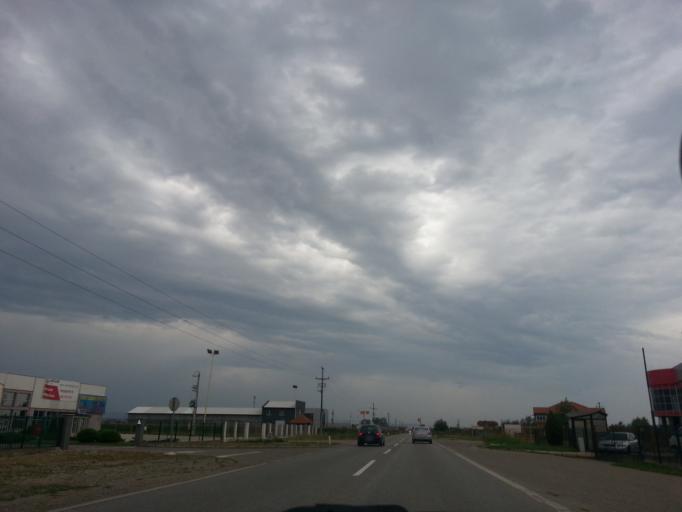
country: BA
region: Republika Srpska
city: Dvorovi
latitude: 44.7861
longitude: 19.2472
